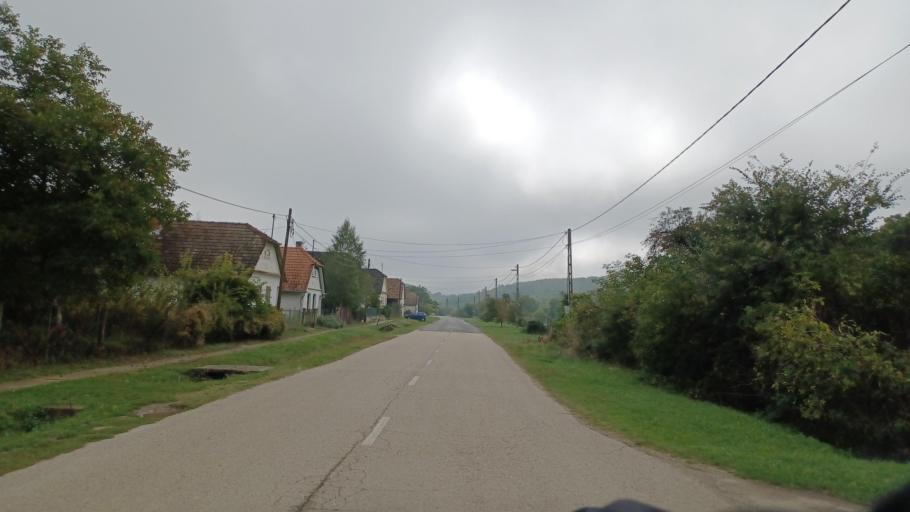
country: HU
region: Tolna
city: Pincehely
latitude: 46.6493
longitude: 18.5190
